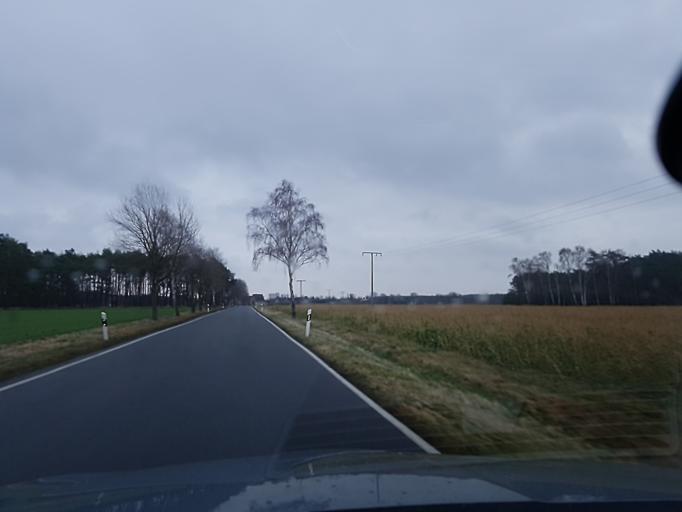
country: DE
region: Brandenburg
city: Schilda
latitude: 51.6123
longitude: 13.3754
